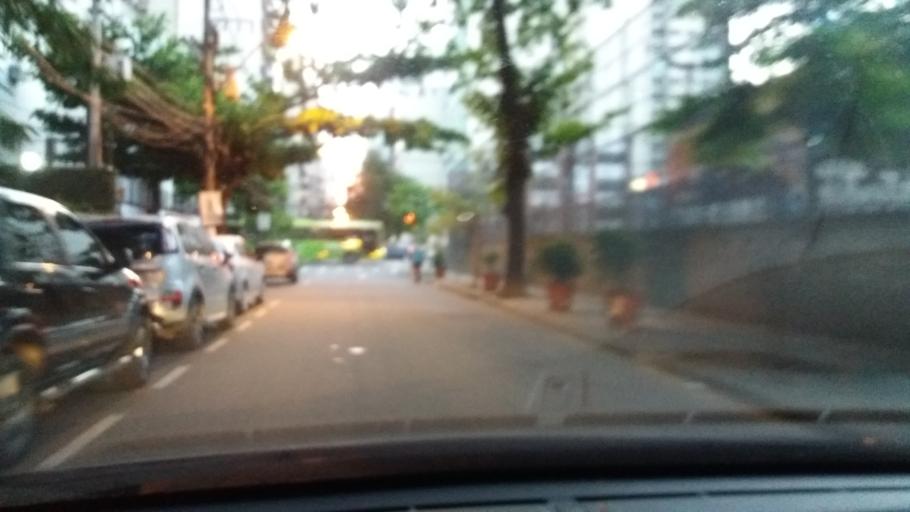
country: BR
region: Rio de Janeiro
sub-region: Niteroi
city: Niteroi
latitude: -22.9005
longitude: -43.1087
